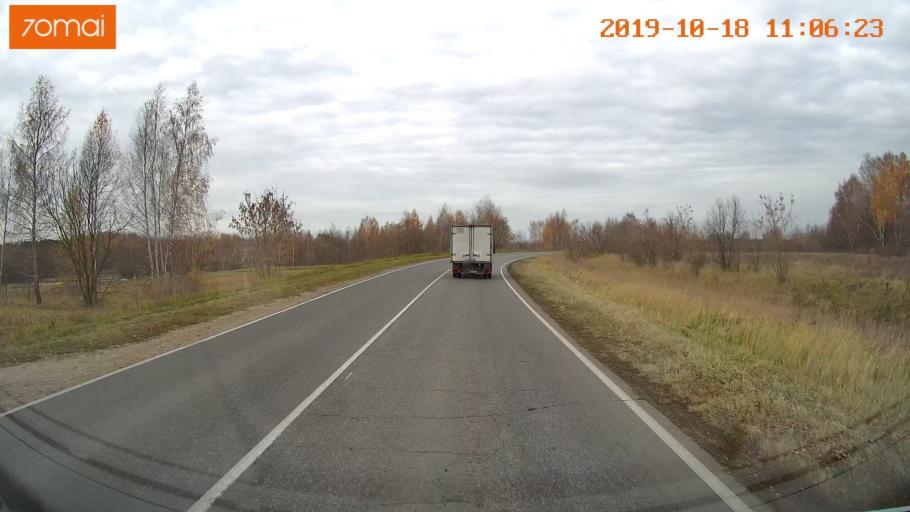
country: RU
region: Tula
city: Kimovsk
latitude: 53.9179
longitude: 38.5375
